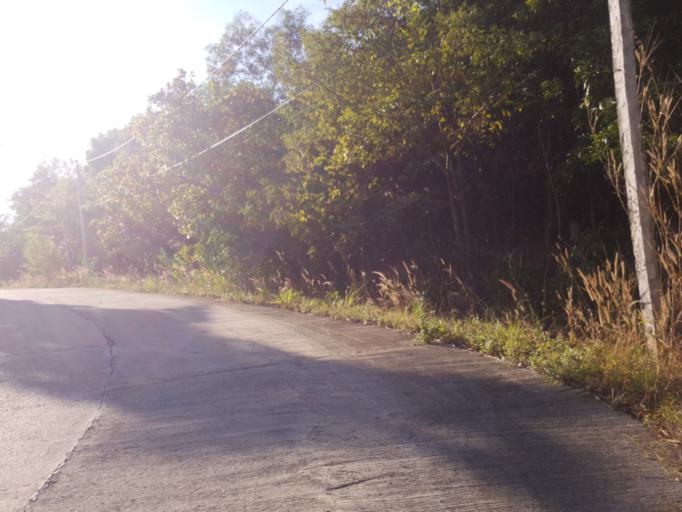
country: VN
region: Kien Giang
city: Duong GJong
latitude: 10.0598
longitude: 104.0350
